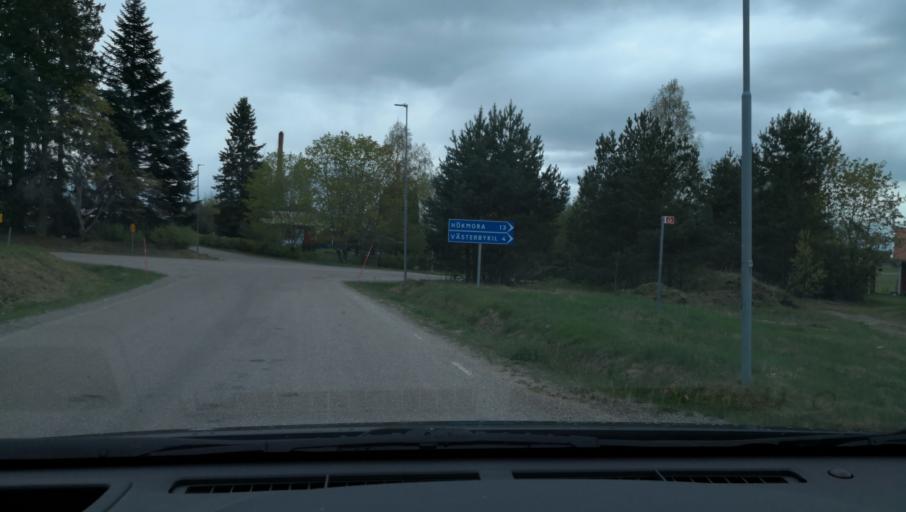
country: SE
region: Dalarna
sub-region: Avesta Kommun
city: Avesta
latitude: 60.0239
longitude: 16.3275
